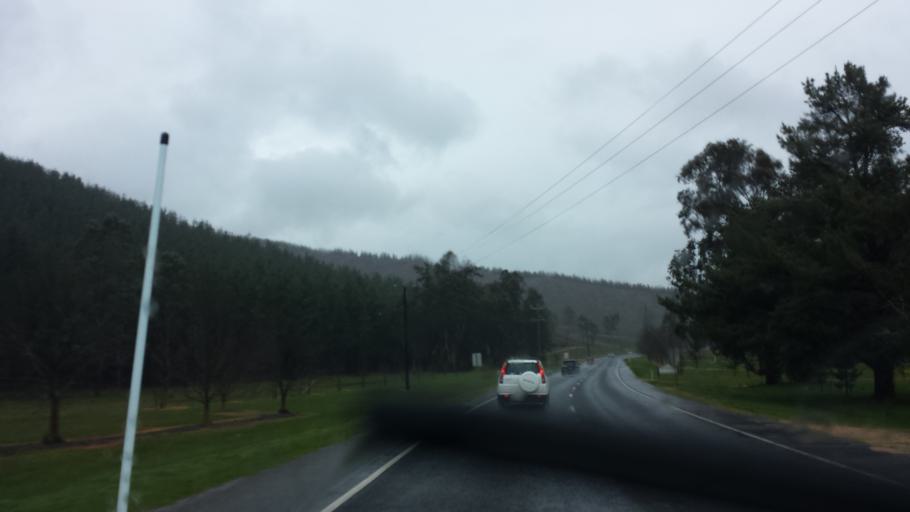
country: AU
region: Victoria
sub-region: Alpine
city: Mount Beauty
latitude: -36.5744
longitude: 146.7457
